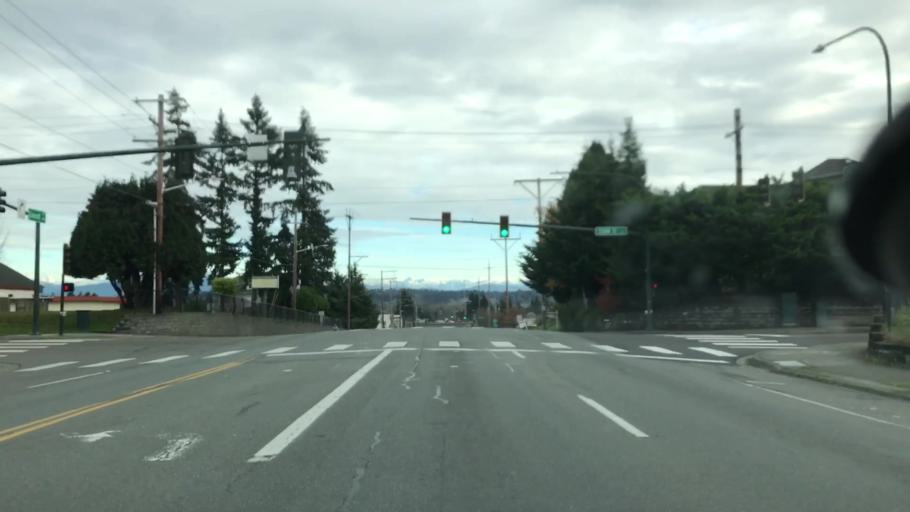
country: US
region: Washington
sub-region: Snohomish County
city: Everett
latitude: 47.9818
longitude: -122.1942
